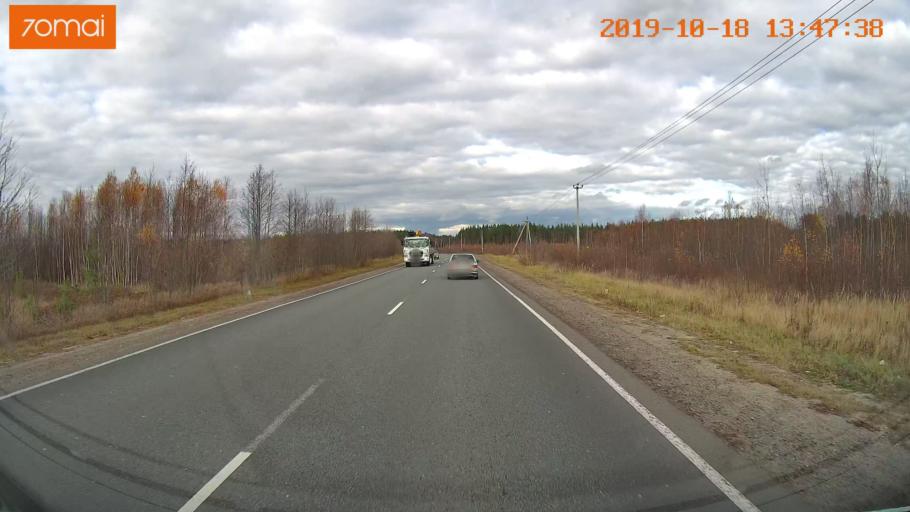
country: RU
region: Moskovskaya
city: Radovitskiy
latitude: 54.9776
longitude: 39.9516
